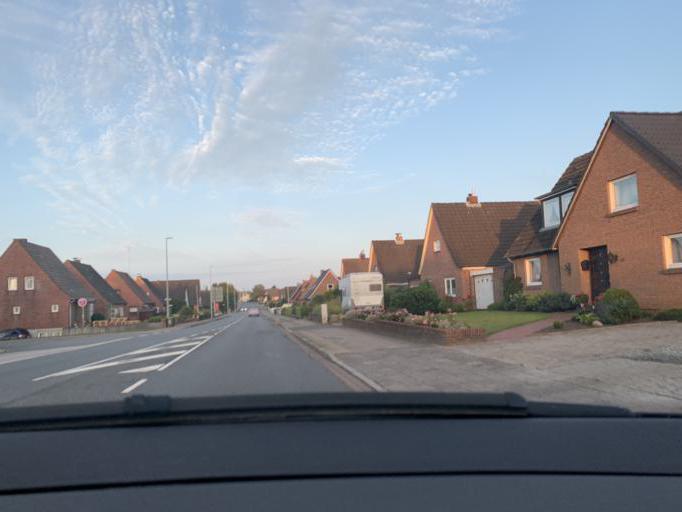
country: DE
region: Schleswig-Holstein
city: Mildstedt
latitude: 54.4719
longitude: 9.0826
